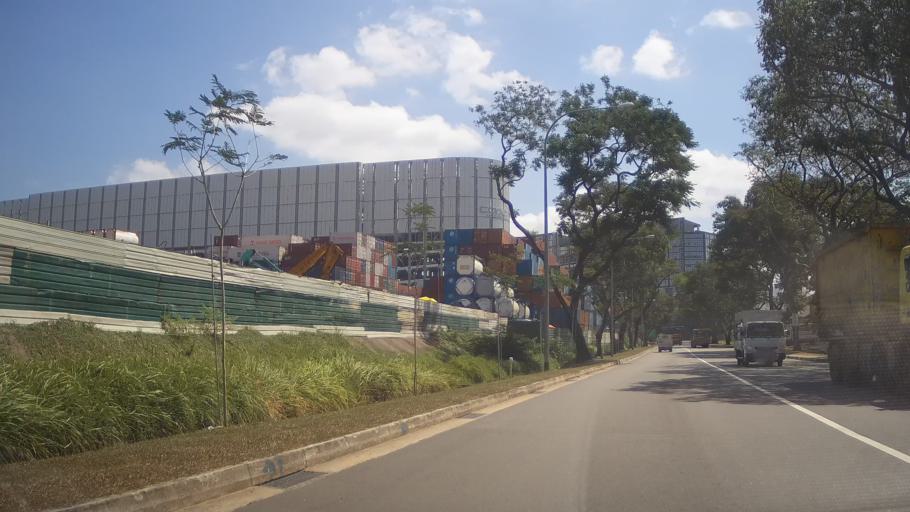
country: SG
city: Singapore
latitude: 1.3077
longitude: 103.6942
